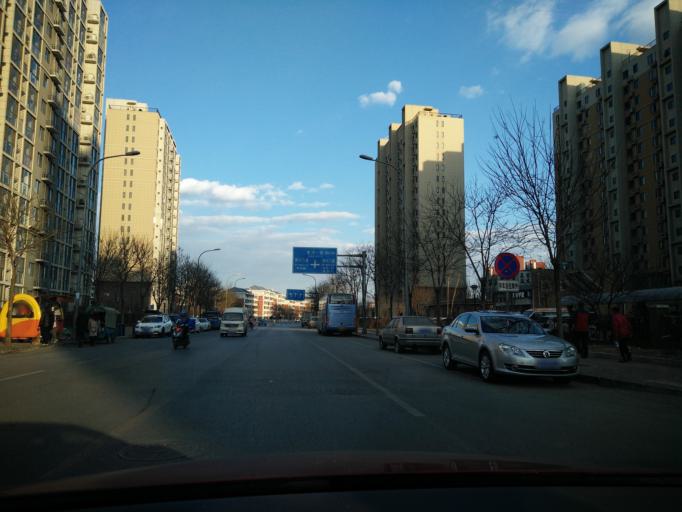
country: CN
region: Beijing
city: Yinghai
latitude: 39.7603
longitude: 116.4899
